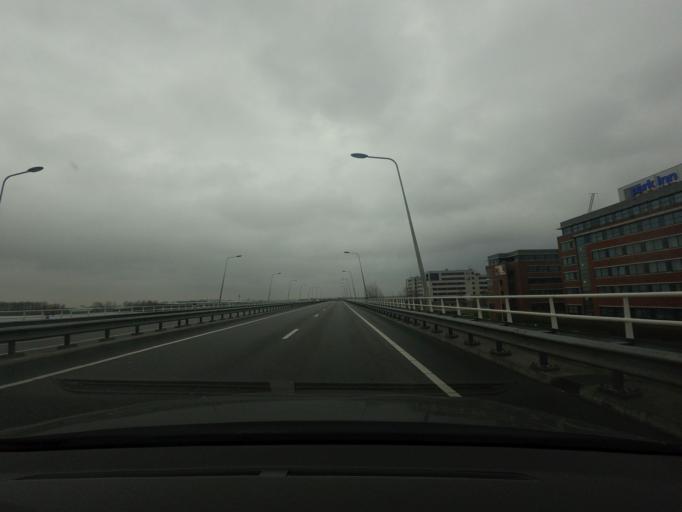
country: NL
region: North Holland
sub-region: Gemeente Aalsmeer
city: Aalsmeer
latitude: 52.2792
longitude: 4.7435
